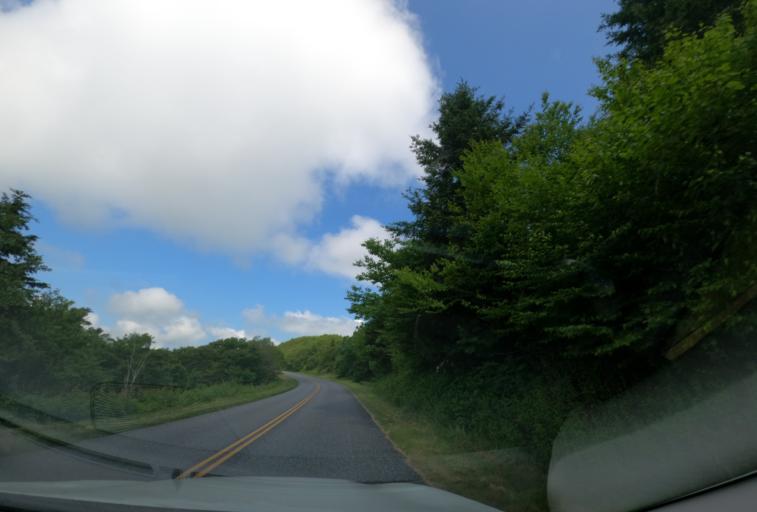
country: US
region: North Carolina
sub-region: Haywood County
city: Hazelwood
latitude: 35.3792
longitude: -83.0221
